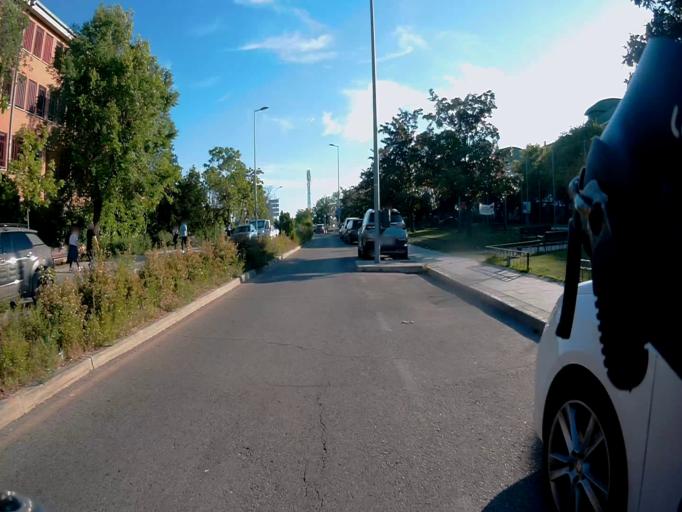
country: ES
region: Madrid
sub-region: Provincia de Madrid
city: Alcorcon
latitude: 40.3407
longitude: -3.8410
